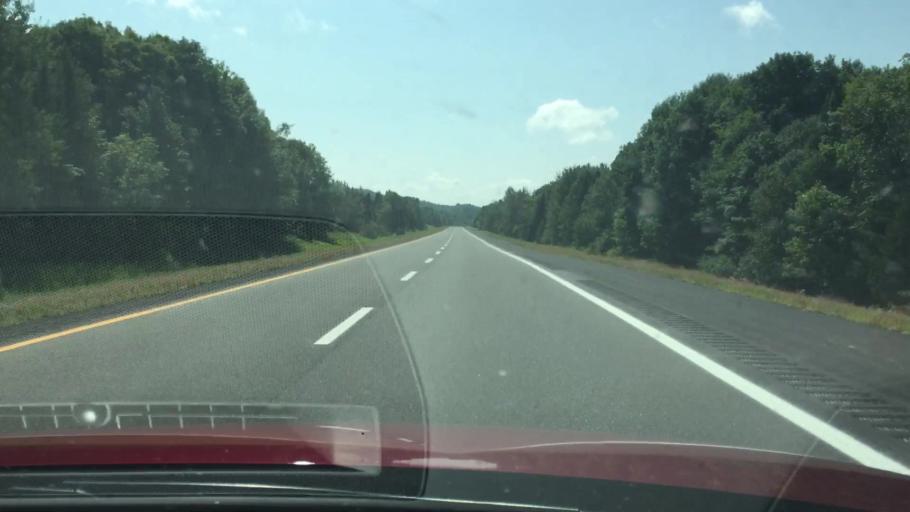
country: US
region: Maine
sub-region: Penobscot County
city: Patten
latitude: 45.9286
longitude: -68.3636
